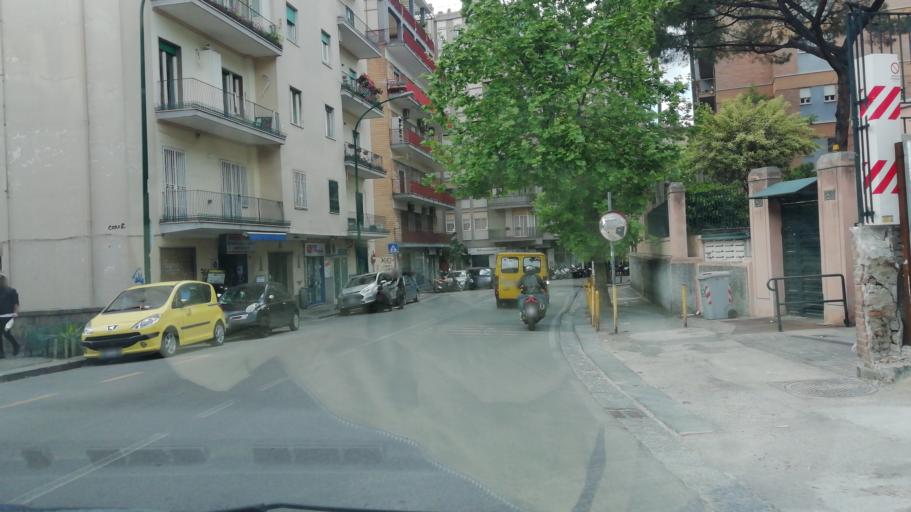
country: IT
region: Campania
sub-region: Provincia di Napoli
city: Napoli
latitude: 40.8553
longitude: 14.2304
